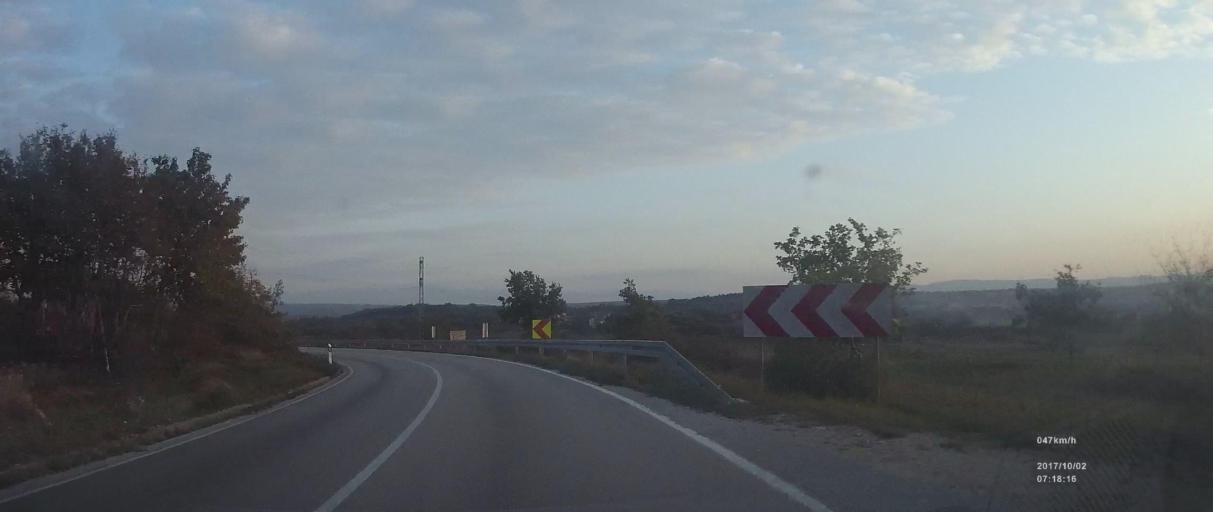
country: HR
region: Zadarska
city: Benkovac
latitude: 44.0166
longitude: 15.5950
